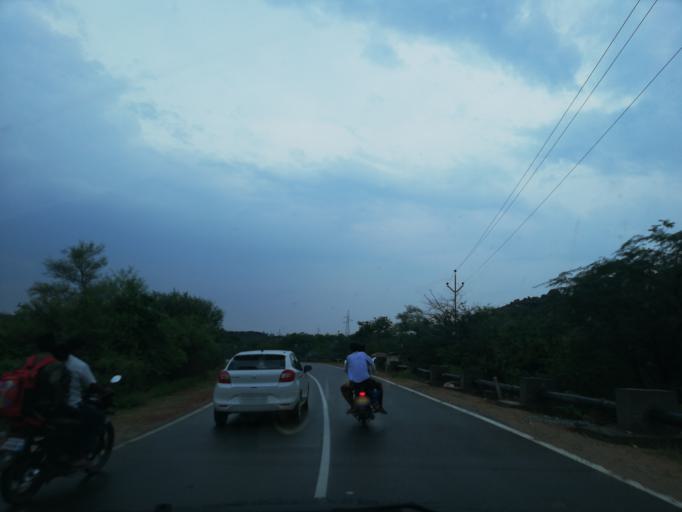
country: IN
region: Andhra Pradesh
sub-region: Guntur
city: Macherla
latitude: 16.6565
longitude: 79.2850
